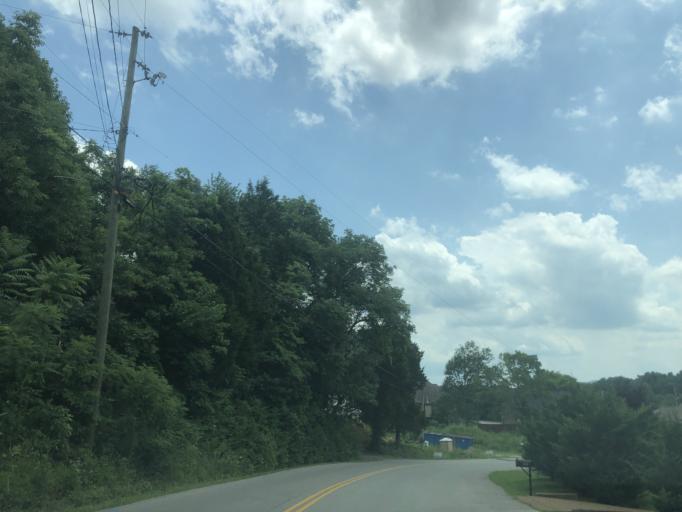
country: US
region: Tennessee
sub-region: Williamson County
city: Brentwood Estates
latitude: 36.0217
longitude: -86.7298
